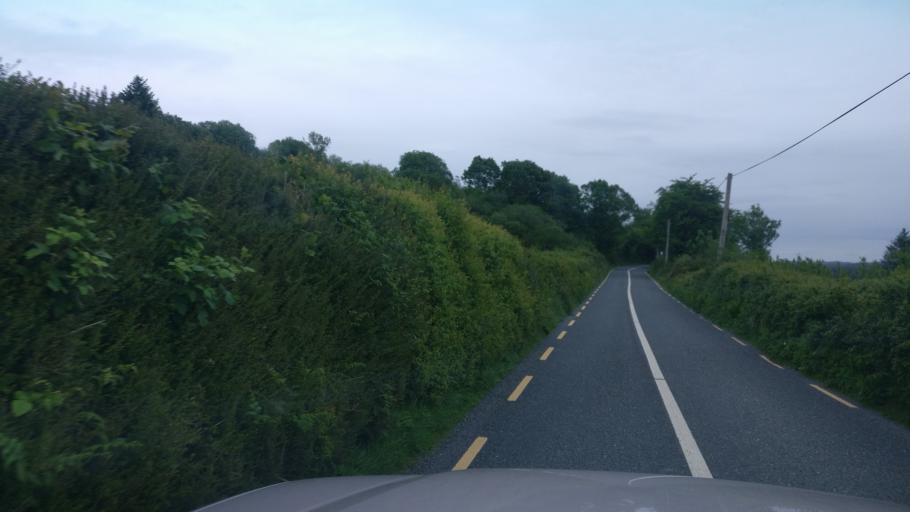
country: IE
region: Connaught
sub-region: County Galway
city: Loughrea
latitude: 53.0555
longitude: -8.6488
